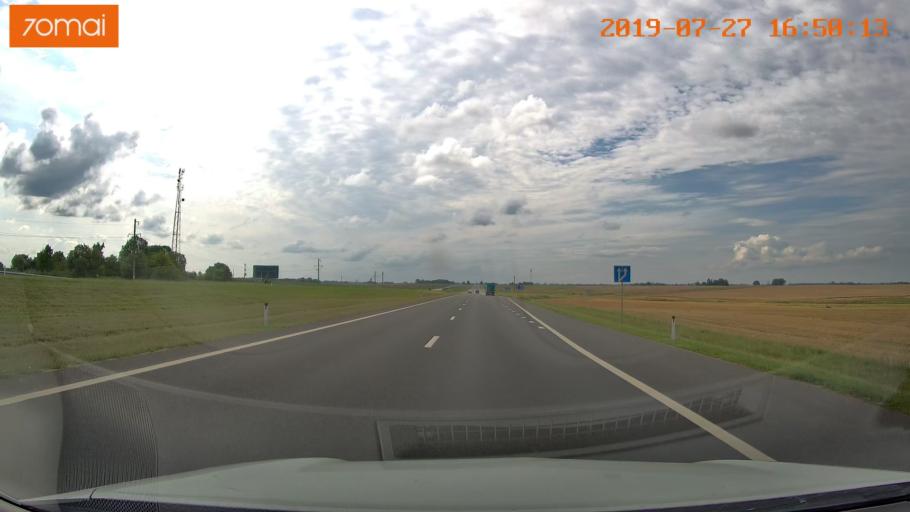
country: RU
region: Kaliningrad
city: Gvardeysk
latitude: 54.6765
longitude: 20.9196
